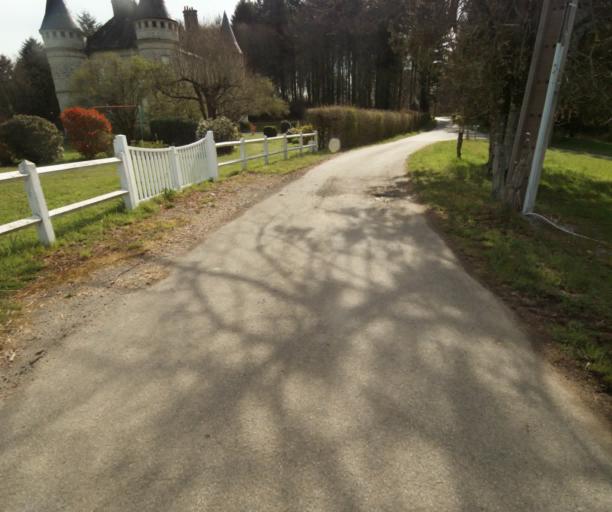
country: FR
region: Limousin
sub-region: Departement de la Correze
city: Correze
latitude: 45.3514
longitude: 1.8711
